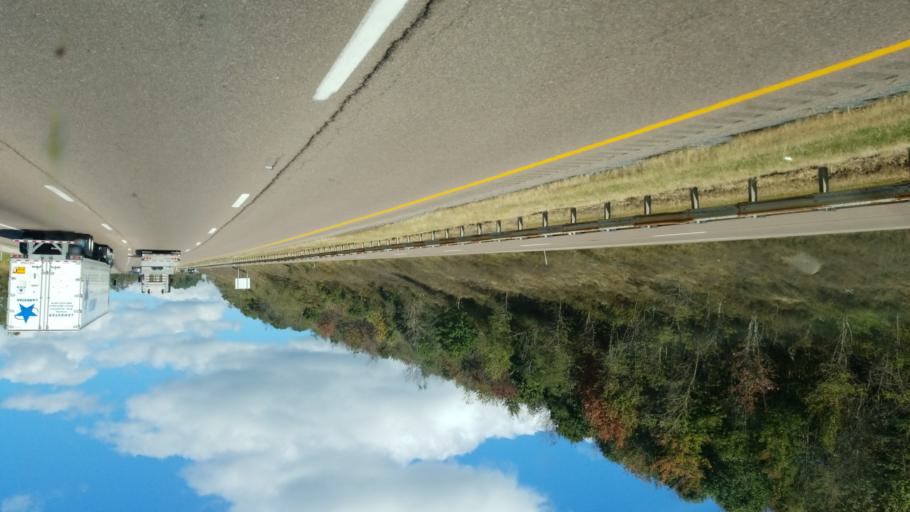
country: US
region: Maryland
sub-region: Allegany County
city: Frostburg
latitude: 39.6502
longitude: -78.9549
